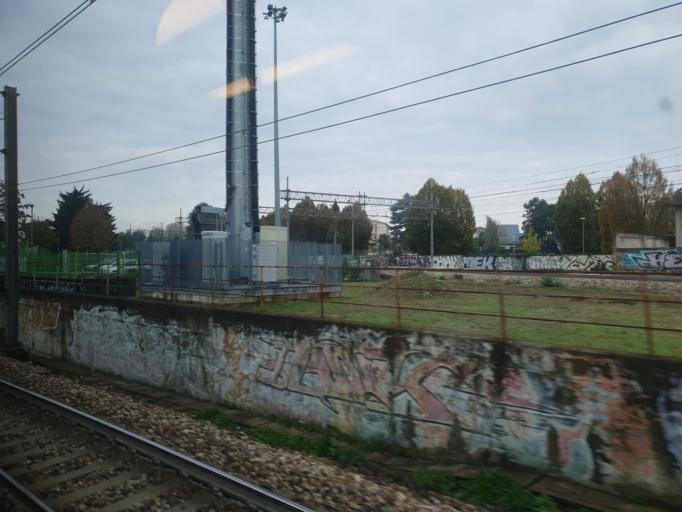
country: IT
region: Lombardy
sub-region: Provincia di Varese
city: Saronno
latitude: 45.6277
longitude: 9.0265
